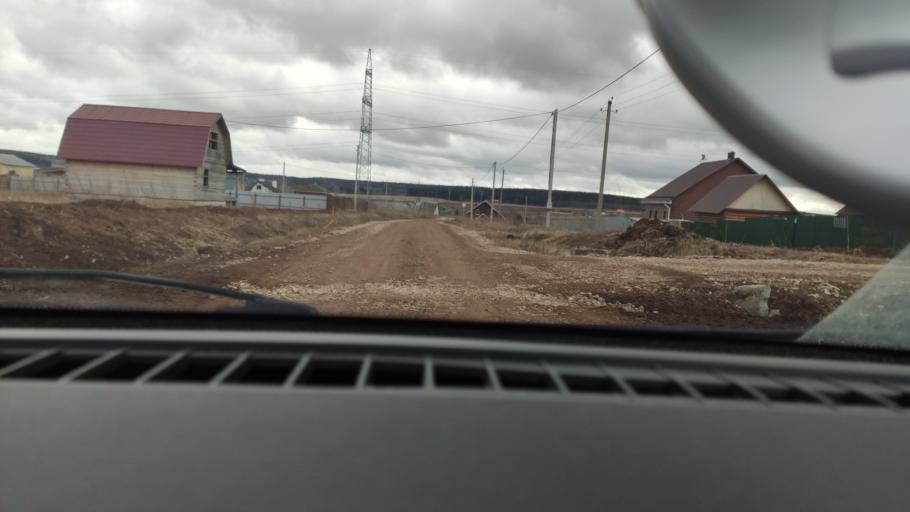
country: RU
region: Perm
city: Ferma
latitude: 57.9446
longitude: 56.3464
